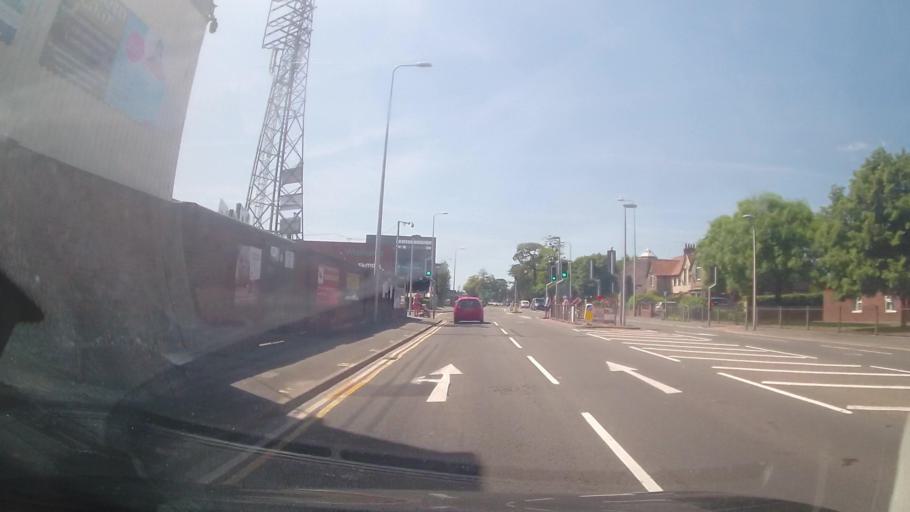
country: GB
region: England
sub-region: Herefordshire
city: Hereford
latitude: 52.0607
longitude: -2.7184
